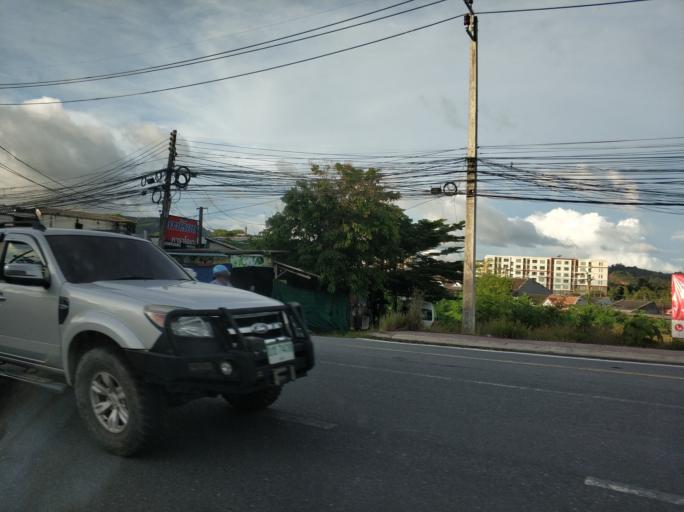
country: TH
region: Phuket
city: Kathu
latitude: 7.9079
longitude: 98.3361
